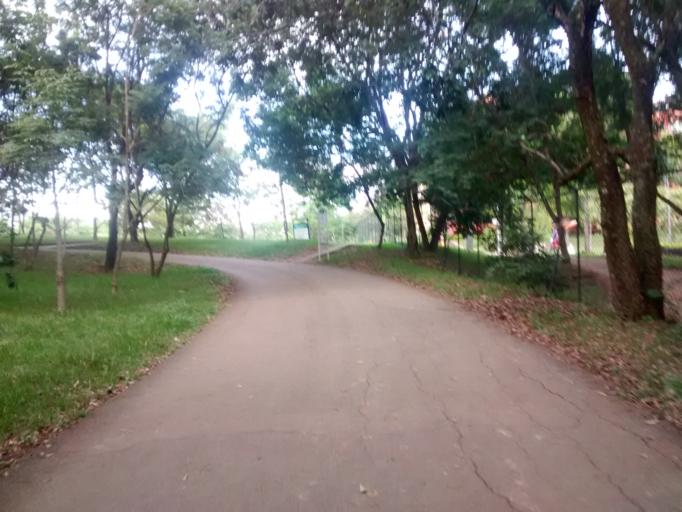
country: BR
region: Federal District
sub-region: Brasilia
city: Brasilia
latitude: -15.7411
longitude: -47.8865
